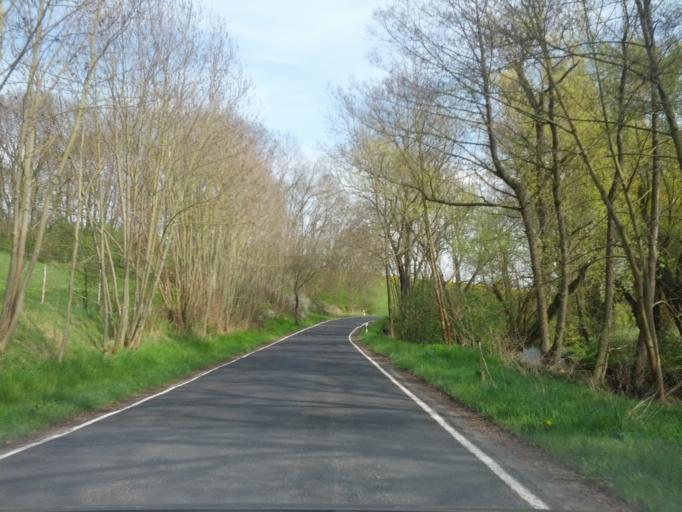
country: DE
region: Thuringia
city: Seebach
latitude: 50.9793
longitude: 10.4403
